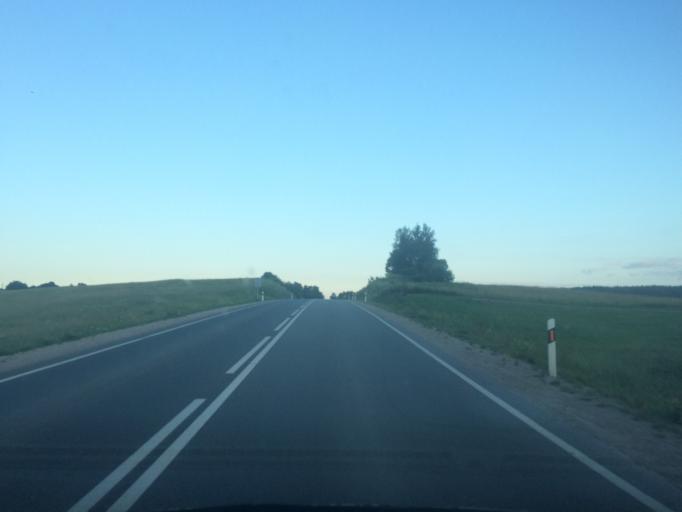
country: LT
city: Zarasai
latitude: 55.7419
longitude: 26.2963
